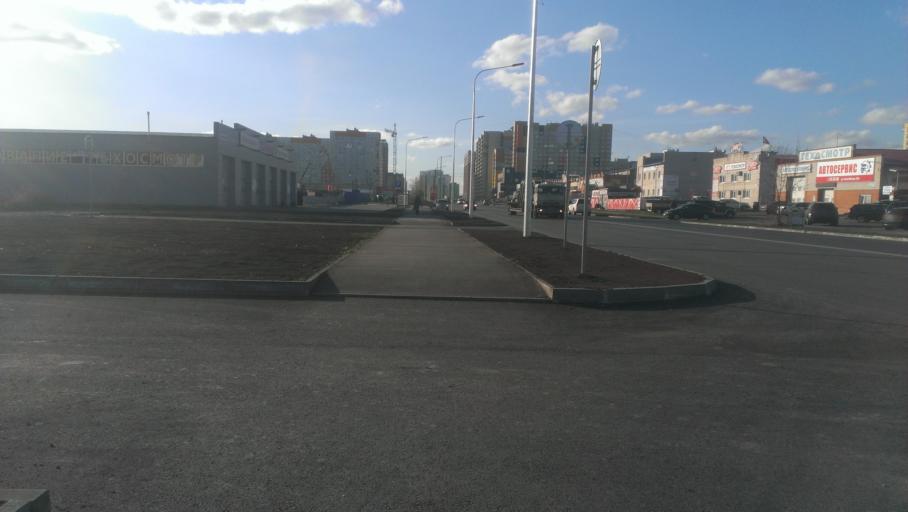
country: RU
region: Altai Krai
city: Novosilikatnyy
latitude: 53.3362
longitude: 83.6671
